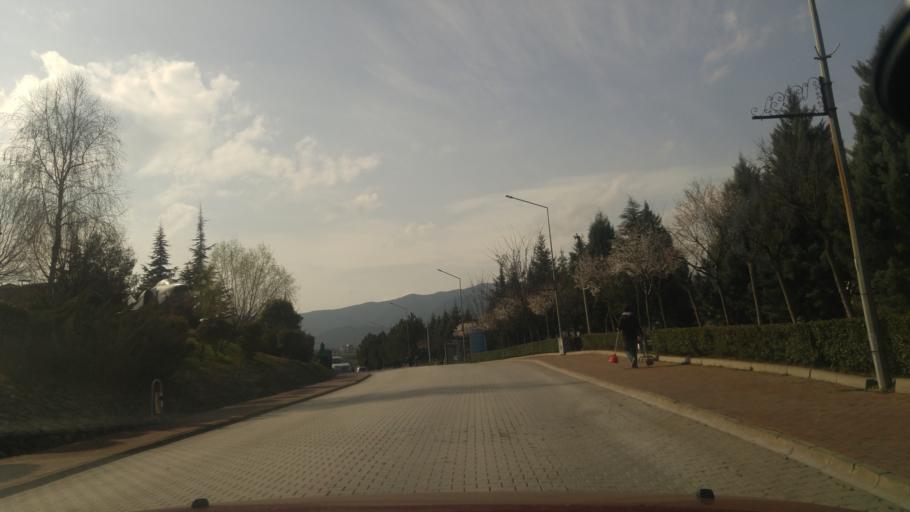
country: TR
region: Karabuk
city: Karabuk
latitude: 41.2146
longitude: 32.6538
